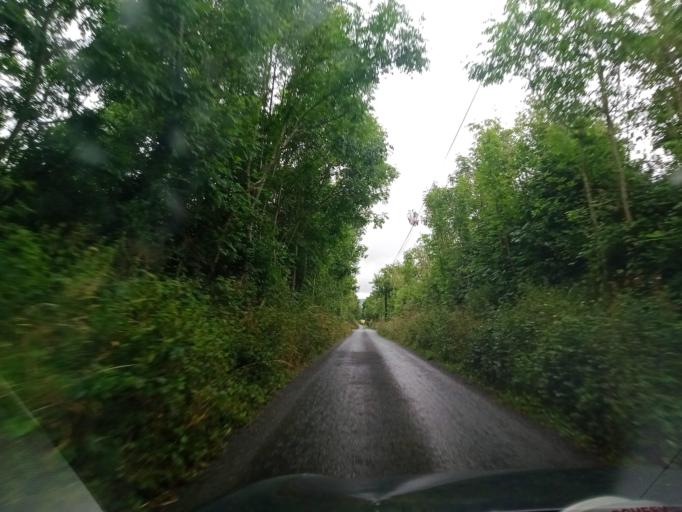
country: IE
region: Leinster
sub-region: Laois
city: Stradbally
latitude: 52.9475
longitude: -7.2352
